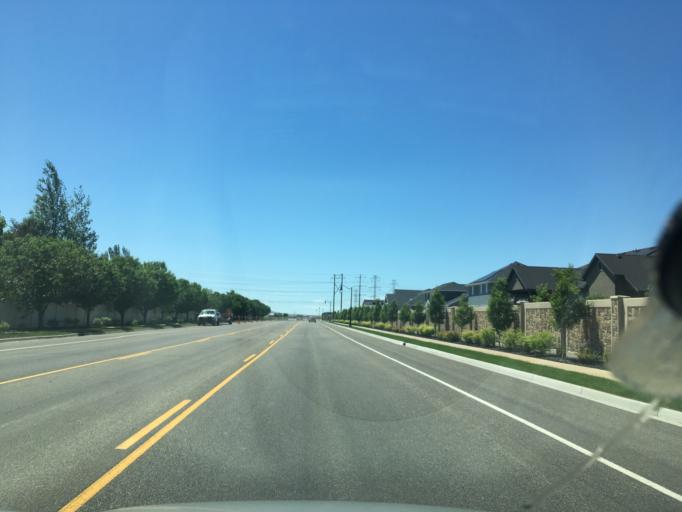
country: US
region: Utah
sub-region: Davis County
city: Layton
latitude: 41.0493
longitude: -111.9944
